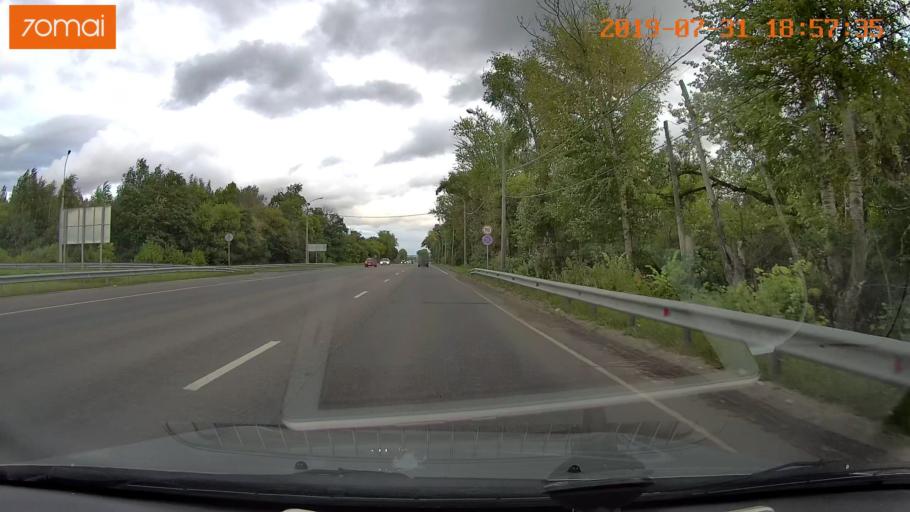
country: RU
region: Moskovskaya
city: Raduzhnyy
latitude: 55.1530
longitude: 38.6940
